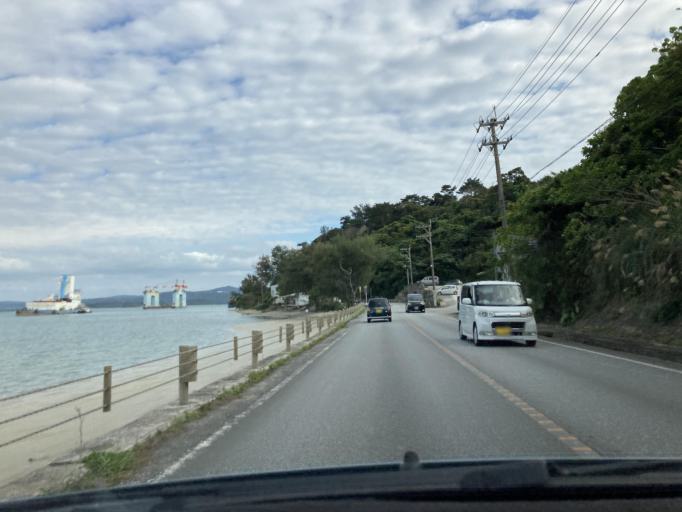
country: JP
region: Okinawa
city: Nago
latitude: 26.6464
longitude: 127.9912
